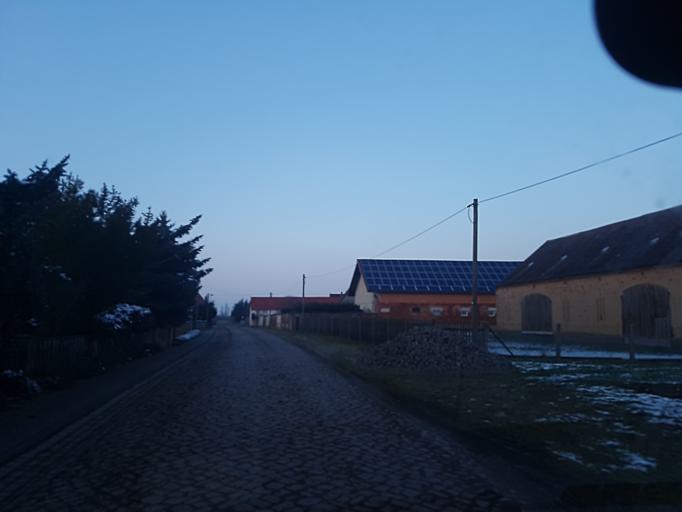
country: DE
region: Brandenburg
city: Muhlberg
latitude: 51.5007
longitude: 13.2820
